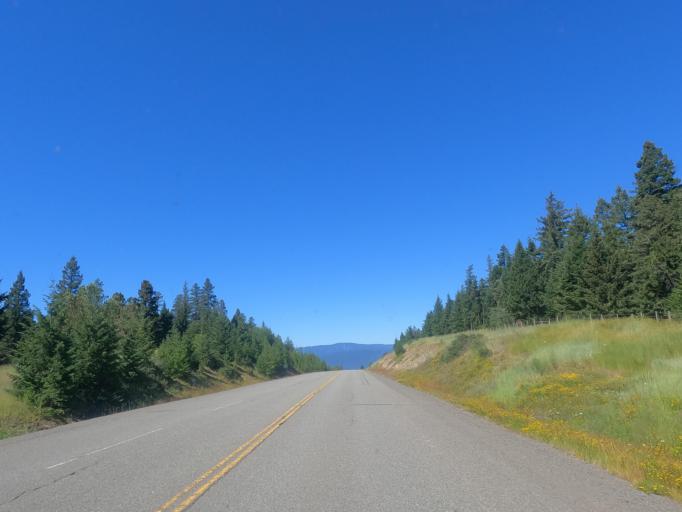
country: CA
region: British Columbia
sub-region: Thompson-Nicola Regional District
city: Ashcroft
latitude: 50.5706
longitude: -121.2022
